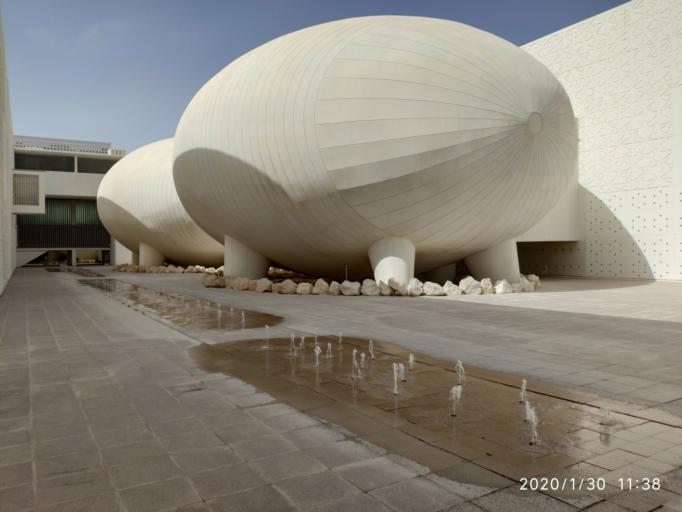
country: QA
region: Baladiyat ar Rayyan
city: Ar Rayyan
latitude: 25.3180
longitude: 51.4398
